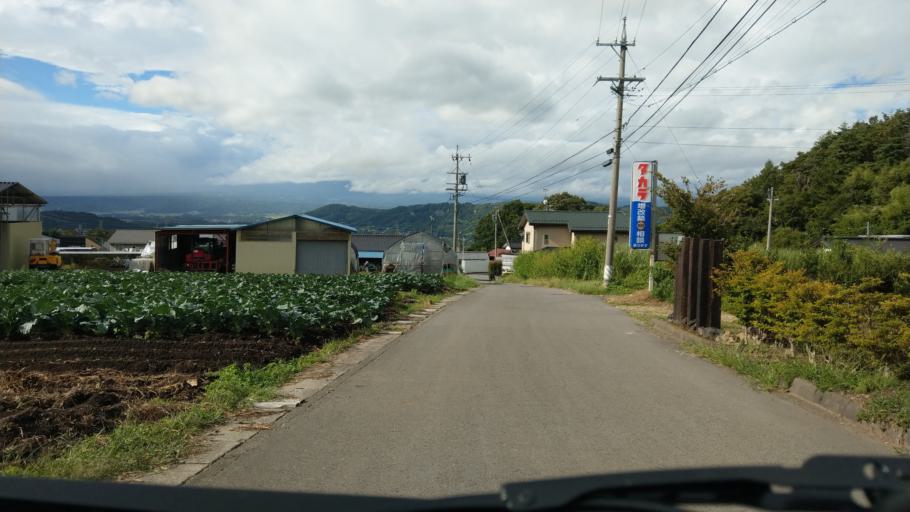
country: JP
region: Nagano
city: Komoro
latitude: 36.3398
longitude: 138.4334
